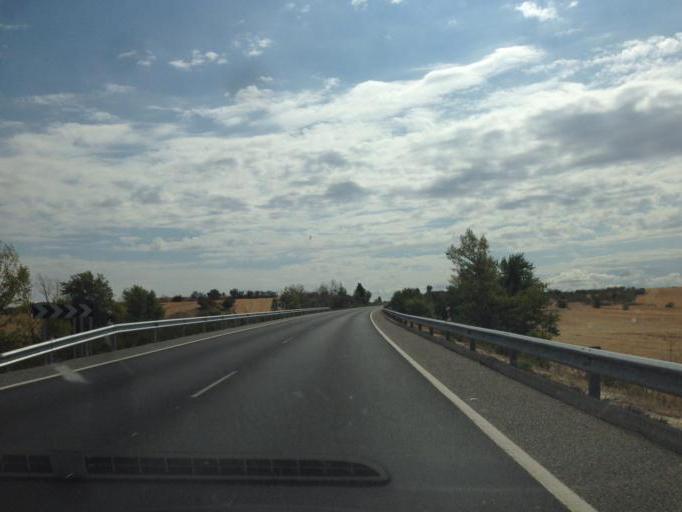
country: ES
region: Madrid
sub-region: Provincia de Madrid
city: Cobena
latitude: 40.5761
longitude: -3.5357
